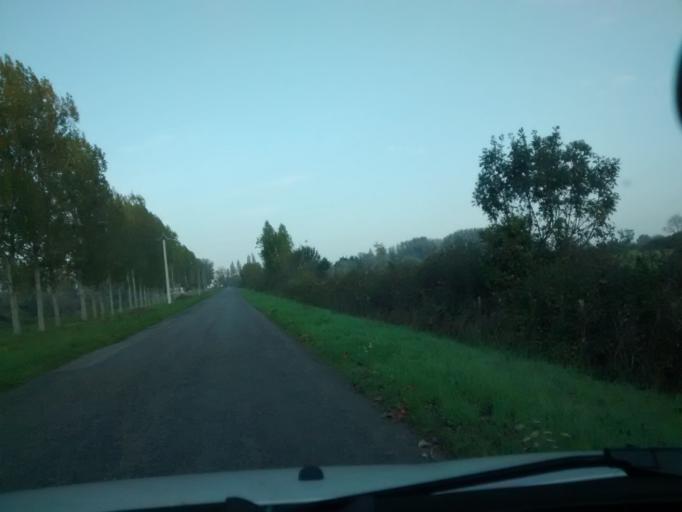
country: FR
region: Pays de la Loire
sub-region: Departement de la Loire-Atlantique
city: Vue
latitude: 47.2352
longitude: -1.8641
